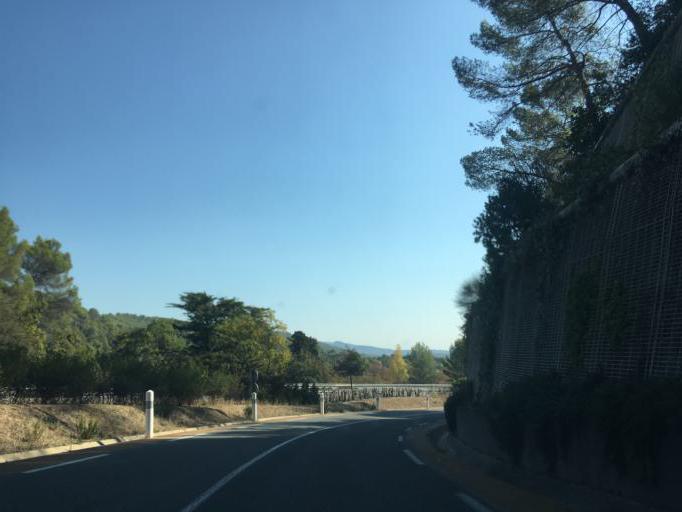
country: FR
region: Provence-Alpes-Cote d'Azur
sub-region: Departement du Var
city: Figanieres
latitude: 43.5719
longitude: 6.5060
